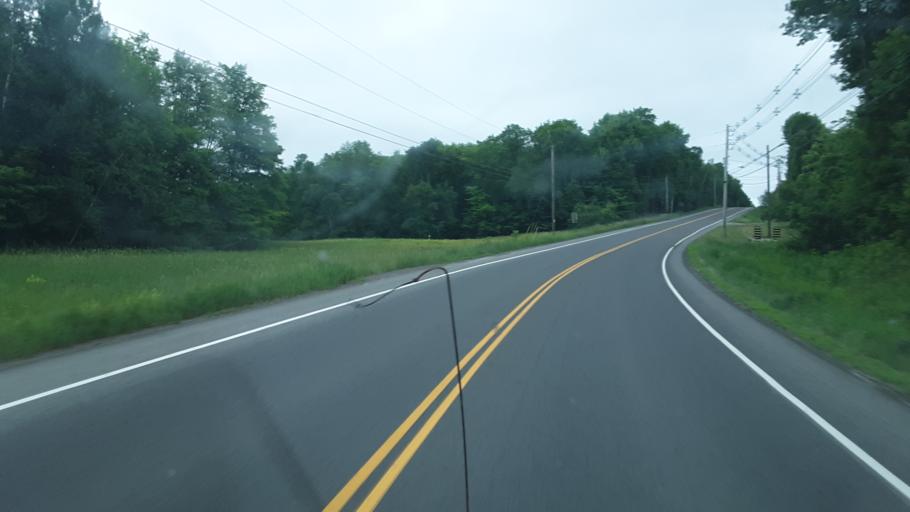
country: US
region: Maine
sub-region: Penobscot County
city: Patten
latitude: 45.8847
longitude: -68.4179
